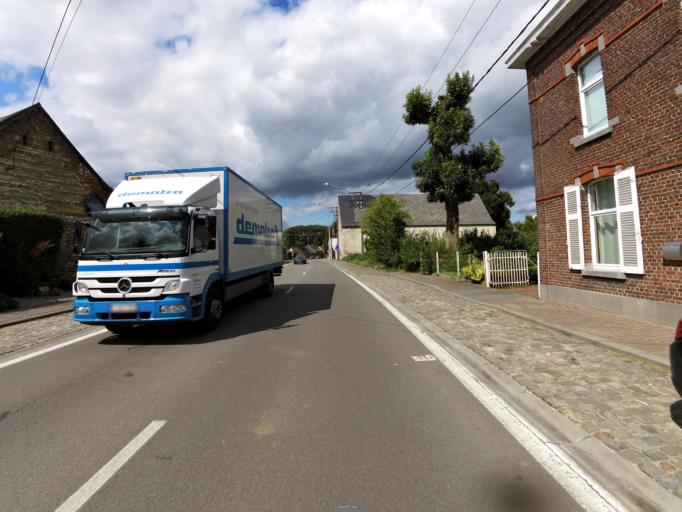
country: BE
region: Wallonia
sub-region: Province du Hainaut
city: Chasse Royale
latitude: 50.4084
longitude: 4.0131
